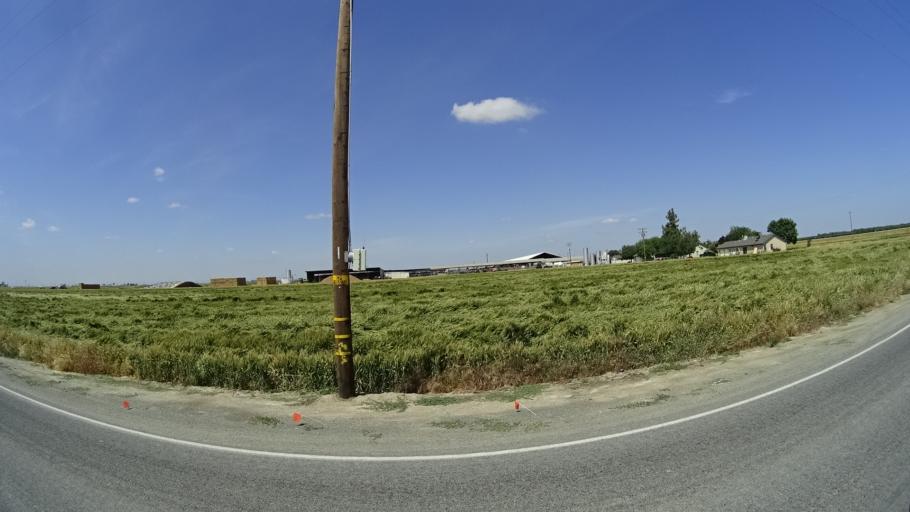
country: US
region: California
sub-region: Tulare County
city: Goshen
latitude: 36.3266
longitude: -119.4931
